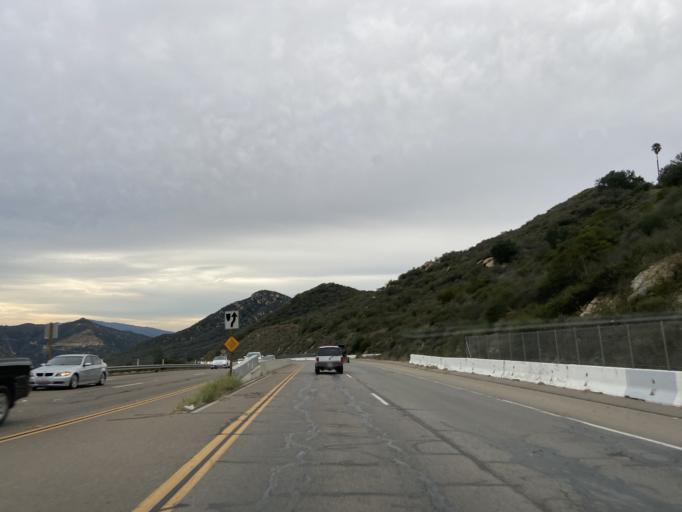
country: US
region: California
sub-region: San Diego County
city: Valley Center
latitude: 33.1983
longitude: -117.0308
